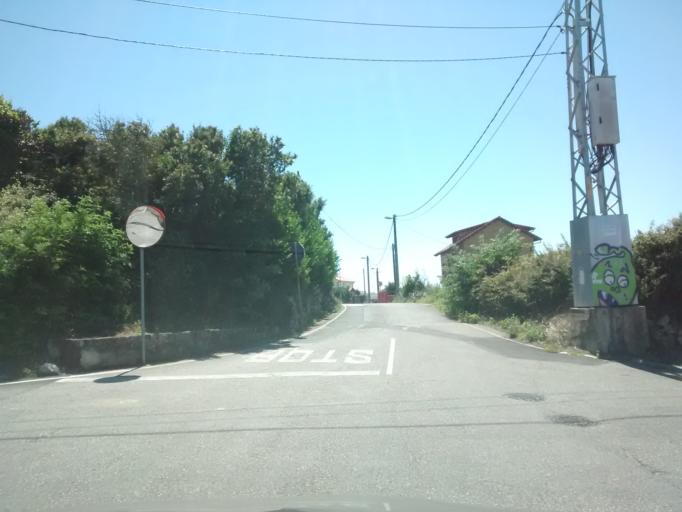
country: ES
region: Cantabria
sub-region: Provincia de Cantabria
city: Santander
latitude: 43.4756
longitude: -3.8221
